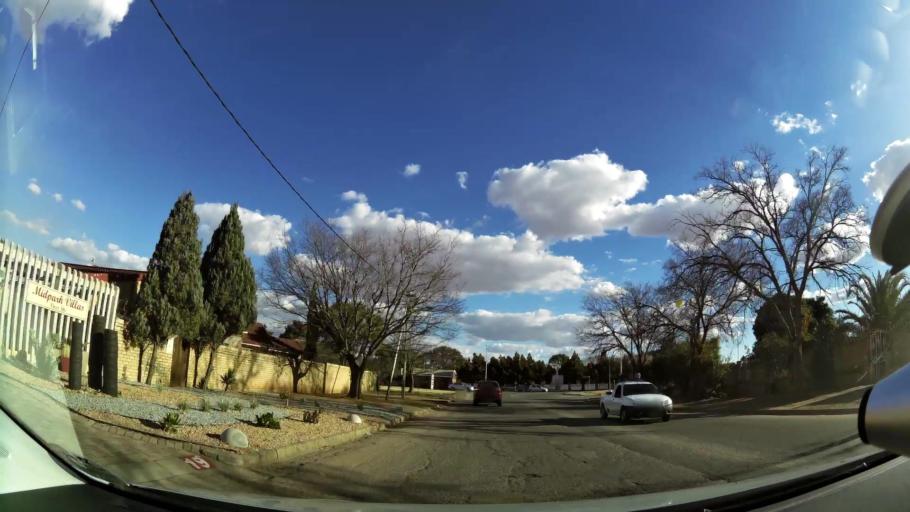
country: ZA
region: North-West
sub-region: Dr Kenneth Kaunda District Municipality
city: Klerksdorp
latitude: -26.8455
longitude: 26.6626
